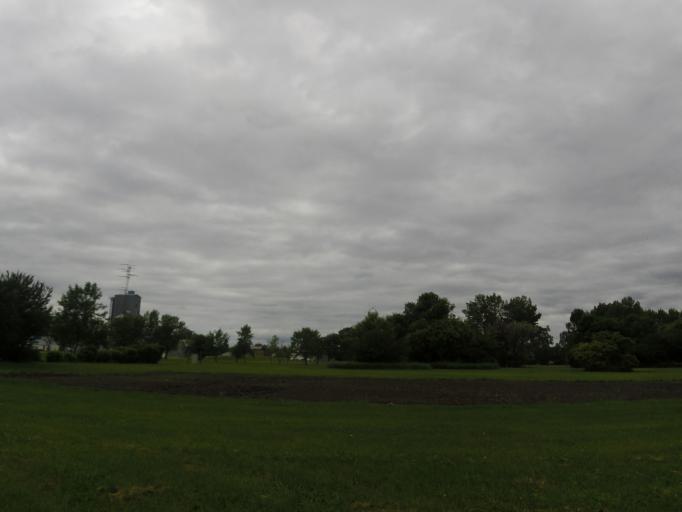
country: US
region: North Dakota
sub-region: Walsh County
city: Grafton
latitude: 48.6199
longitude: -97.4434
